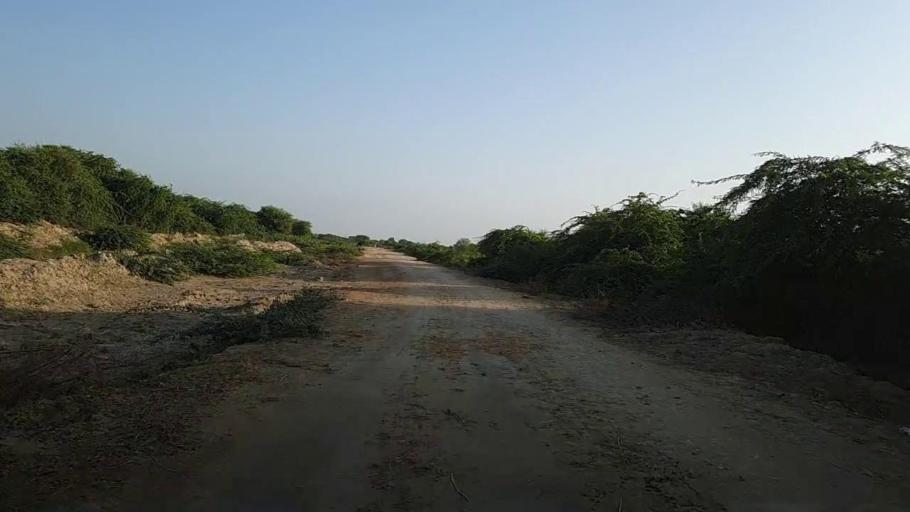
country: PK
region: Sindh
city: Kario
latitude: 24.7076
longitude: 68.6668
